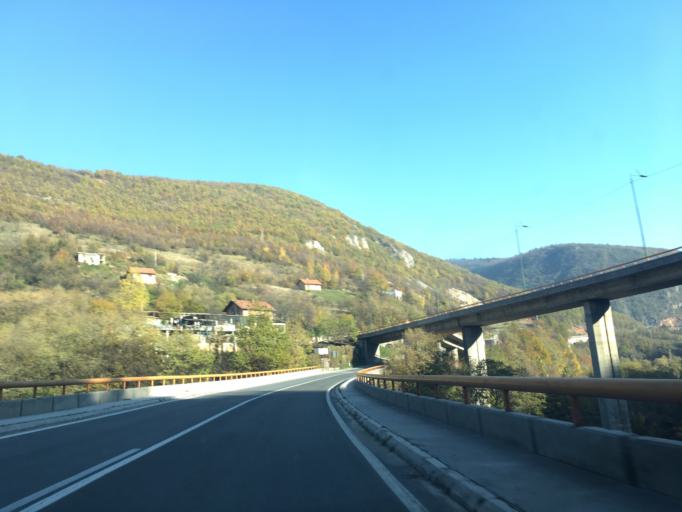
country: BA
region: Federation of Bosnia and Herzegovina
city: Kobilja Glava
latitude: 43.8575
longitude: 18.4501
